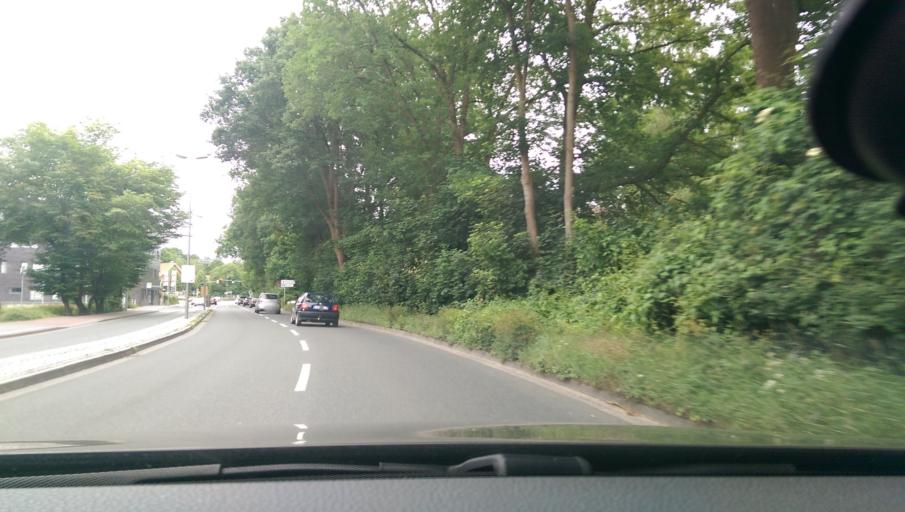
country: DE
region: Lower Saxony
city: Rotenburg
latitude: 53.1089
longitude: 9.3962
